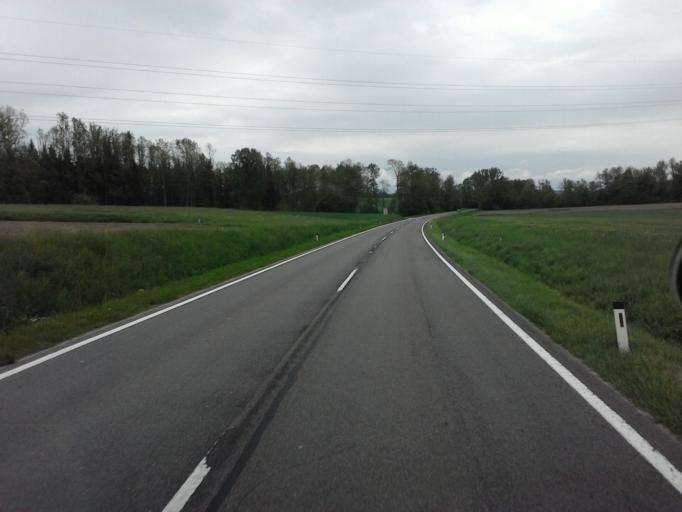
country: AT
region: Upper Austria
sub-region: Politischer Bezirk Vocklabruck
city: Wolfsegg am Hausruck
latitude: 48.2098
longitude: 13.6812
